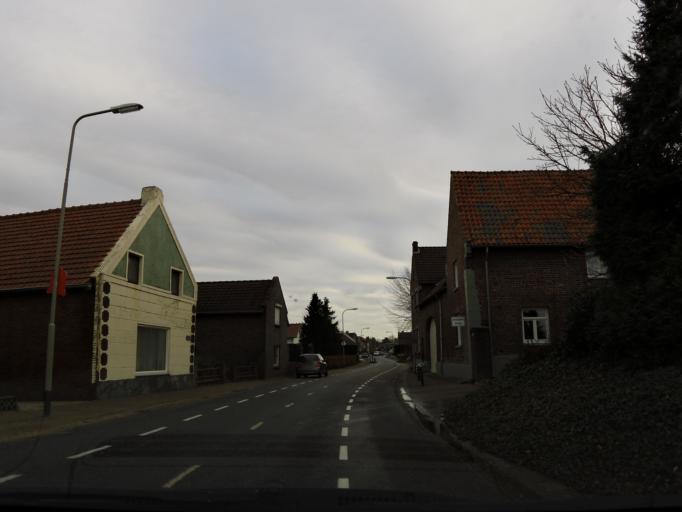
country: NL
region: Limburg
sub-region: Gemeente Schinnen
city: Puth
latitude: 50.9397
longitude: 5.8608
